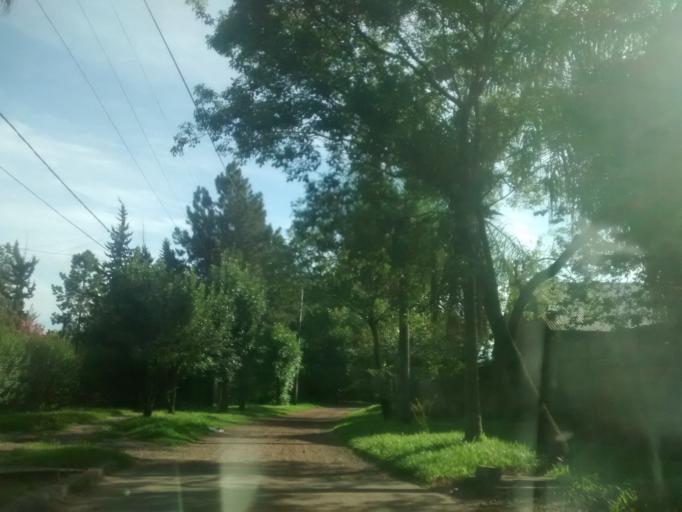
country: AR
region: Chaco
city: Puerto Tirol
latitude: -27.3711
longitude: -59.0883
